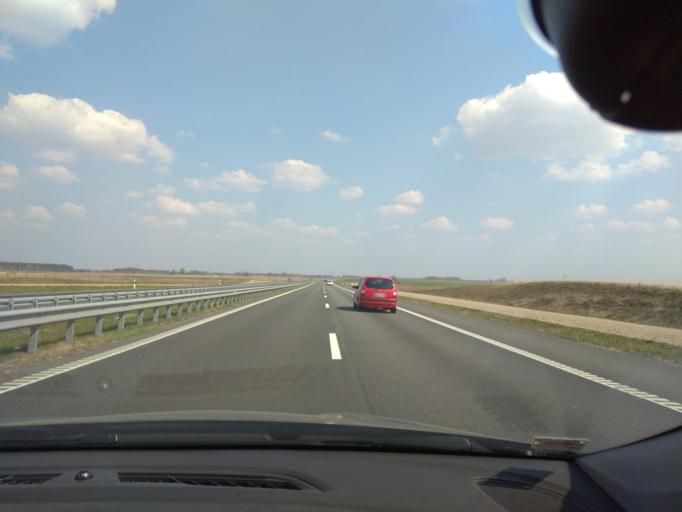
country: LT
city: Kazlu Ruda
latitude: 54.6939
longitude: 23.6019
